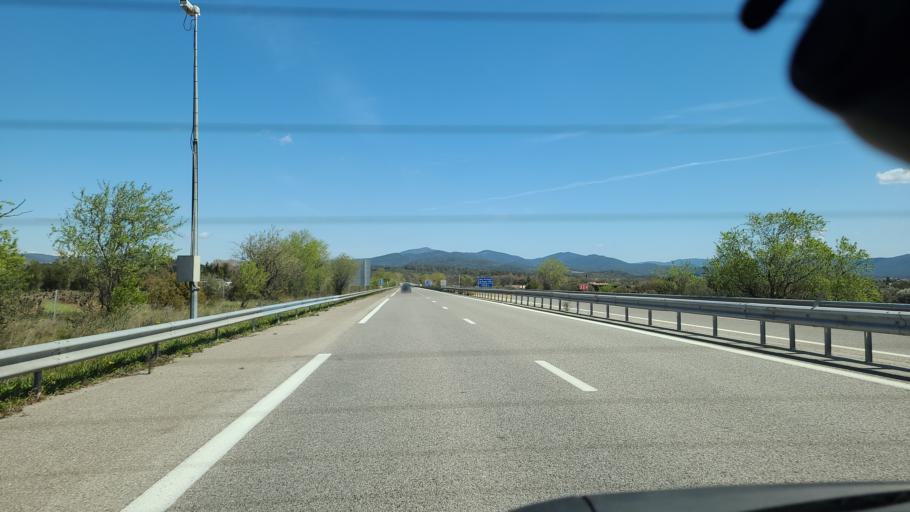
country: FR
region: Provence-Alpes-Cote d'Azur
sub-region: Departement du Var
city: Cuers
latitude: 43.2522
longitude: 6.1031
